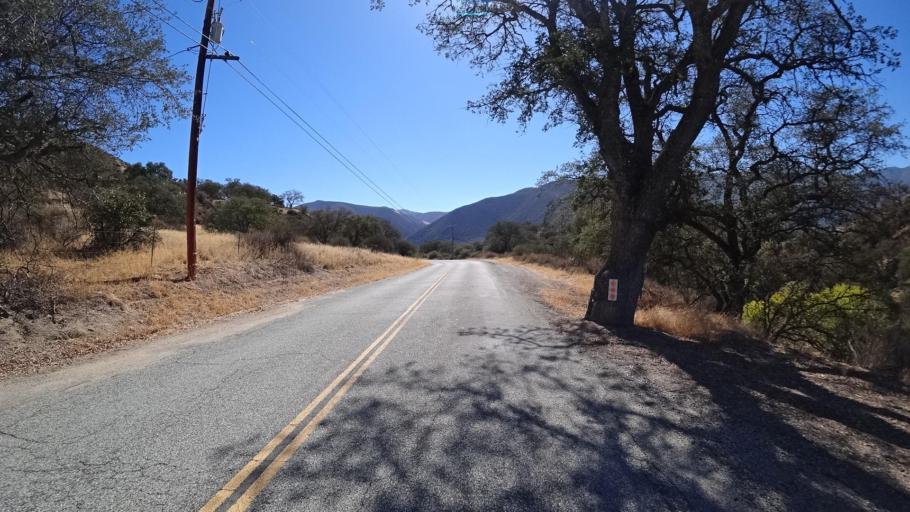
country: US
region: California
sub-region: Monterey County
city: Soledad
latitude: 36.2628
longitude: -121.4281
